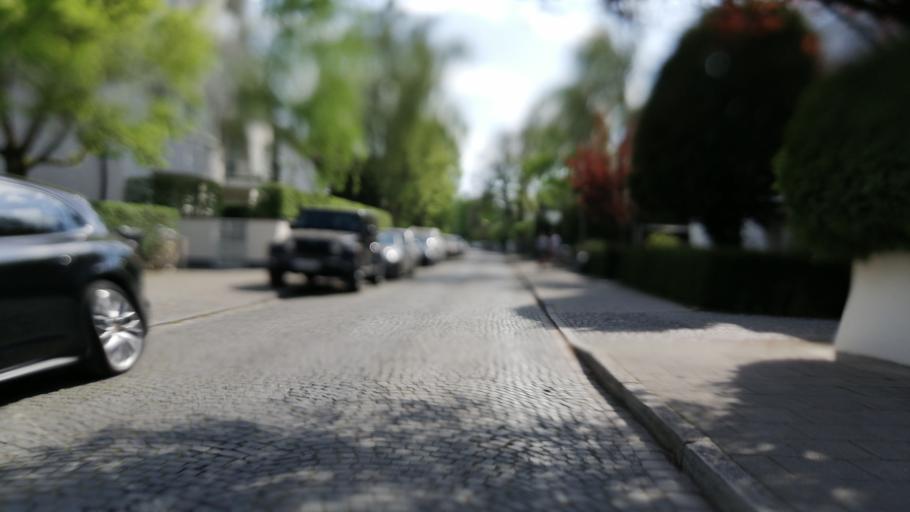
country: DE
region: Bavaria
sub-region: Upper Bavaria
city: Bogenhausen
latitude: 48.1591
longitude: 11.6134
